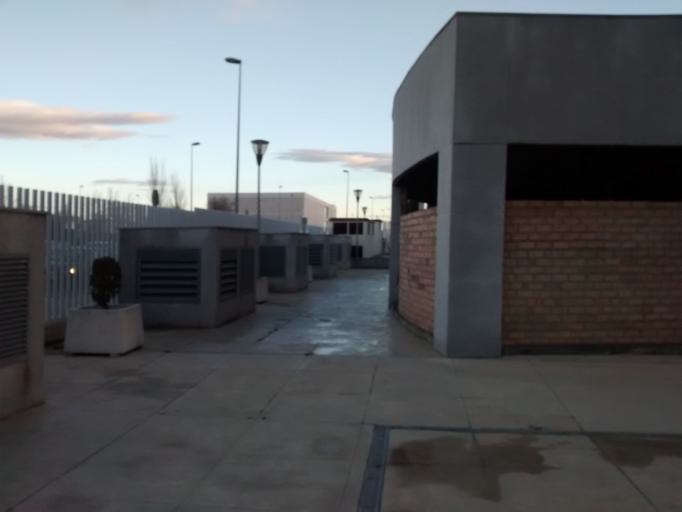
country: ES
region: Andalusia
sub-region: Provincia de Sevilla
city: Sevilla
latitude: 37.4254
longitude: -5.9750
